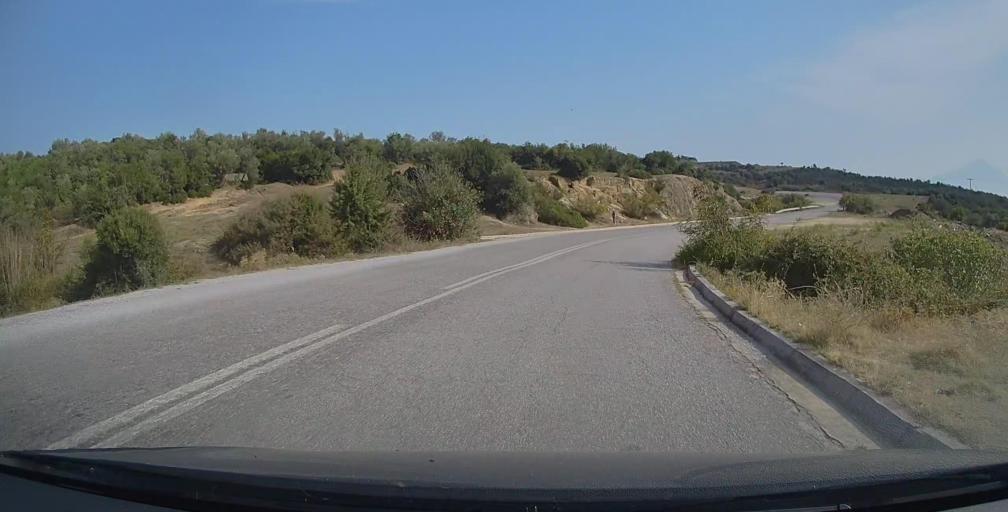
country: GR
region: Central Macedonia
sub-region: Nomos Chalkidikis
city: Sykia
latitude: 40.0219
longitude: 23.9867
